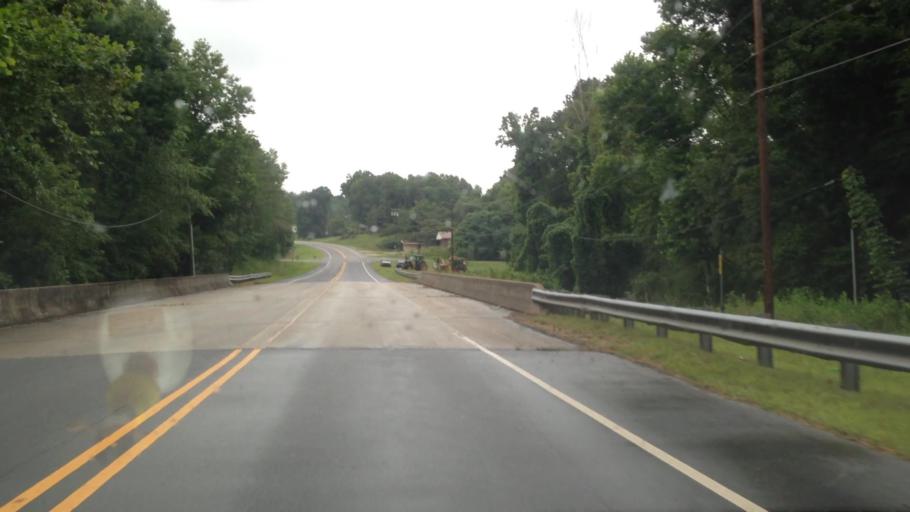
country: US
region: North Carolina
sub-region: Rockingham County
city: Mayodan
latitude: 36.4087
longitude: -79.9882
